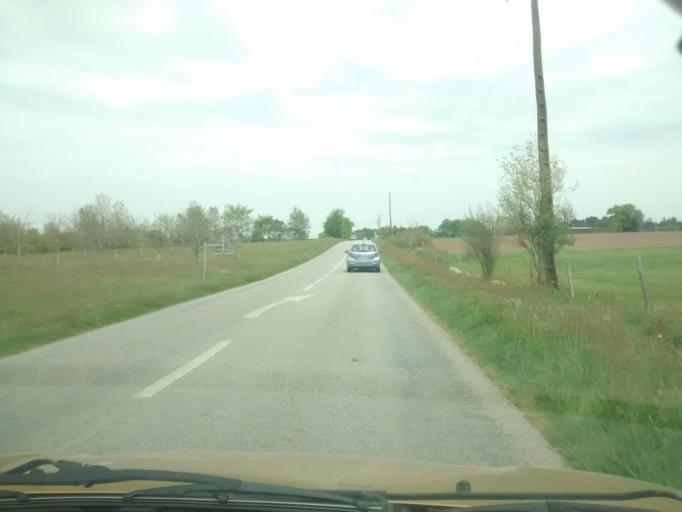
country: FR
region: Brittany
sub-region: Departement du Morbihan
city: Questembert
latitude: 47.6576
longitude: -2.4785
